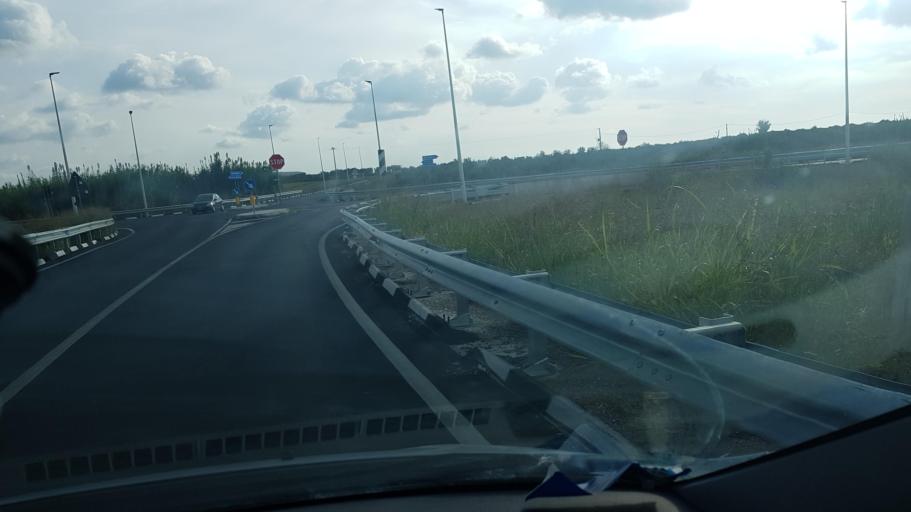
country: IT
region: Apulia
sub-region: Provincia di Brindisi
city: Cellino San Marco
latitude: 40.4393
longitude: 17.9551
